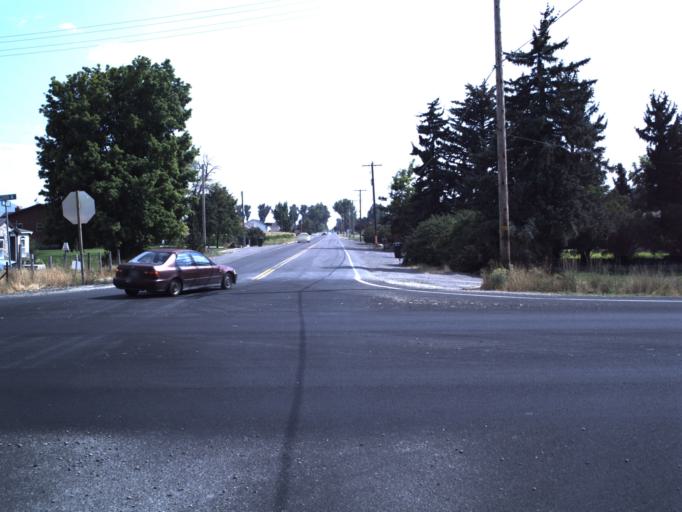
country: US
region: Utah
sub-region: Box Elder County
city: Garland
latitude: 41.7866
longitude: -112.1252
